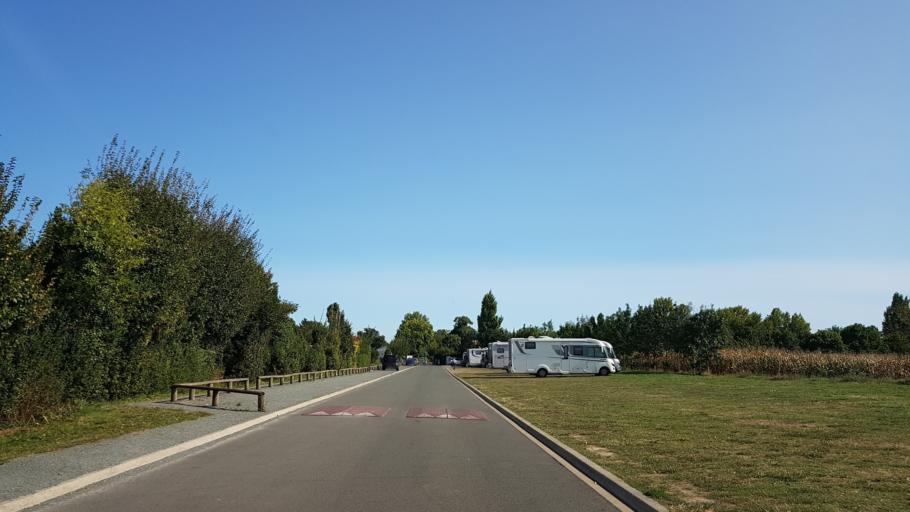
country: FR
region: Poitou-Charentes
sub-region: Departement de la Charente-Maritime
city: Breuillet
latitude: 45.7086
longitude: -1.0323
